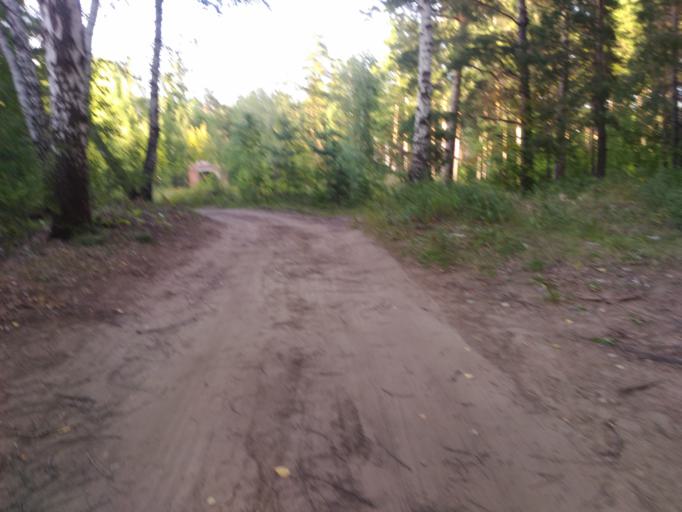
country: RU
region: Ulyanovsk
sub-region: Ulyanovskiy Rayon
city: Ulyanovsk
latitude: 54.3564
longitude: 48.5172
